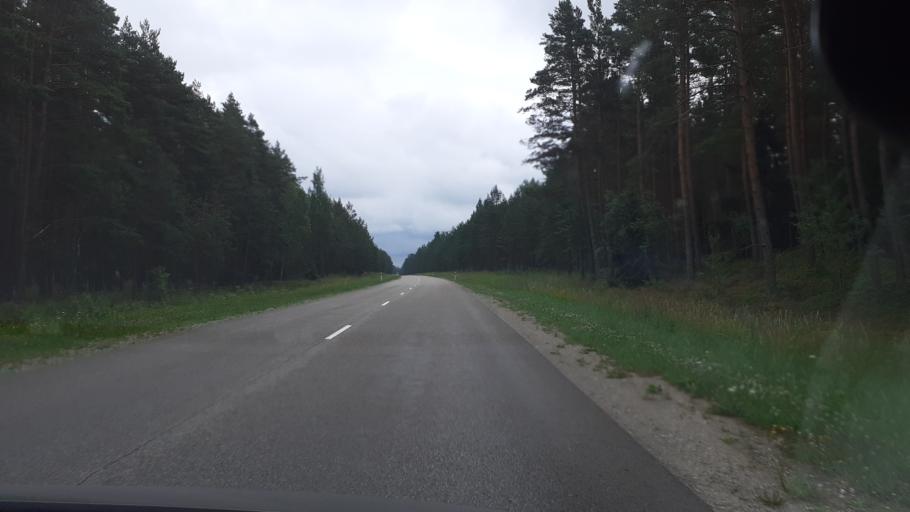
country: LV
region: Ventspils Rajons
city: Piltene
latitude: 57.1177
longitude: 21.7494
